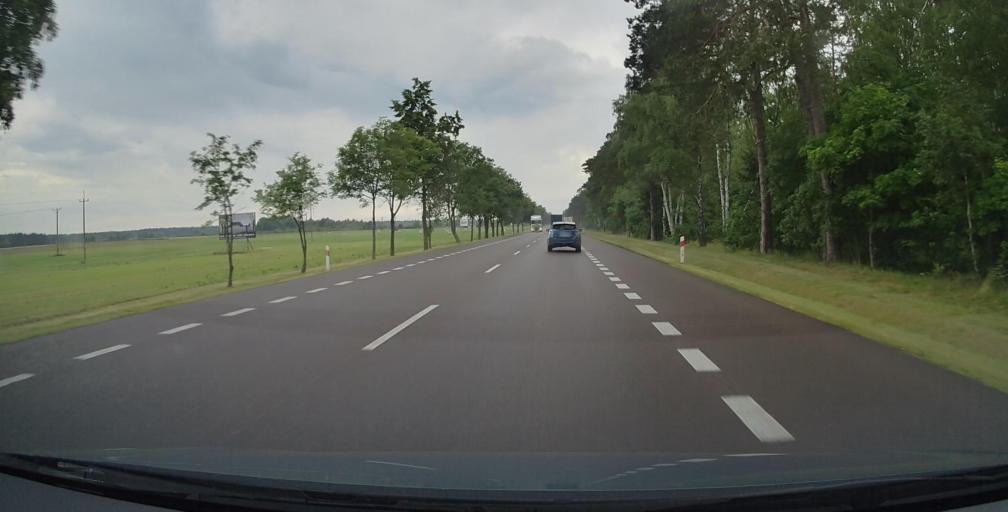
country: PL
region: Lublin Voivodeship
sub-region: Powiat bialski
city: Lesna Podlaska
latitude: 52.0380
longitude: 22.9631
